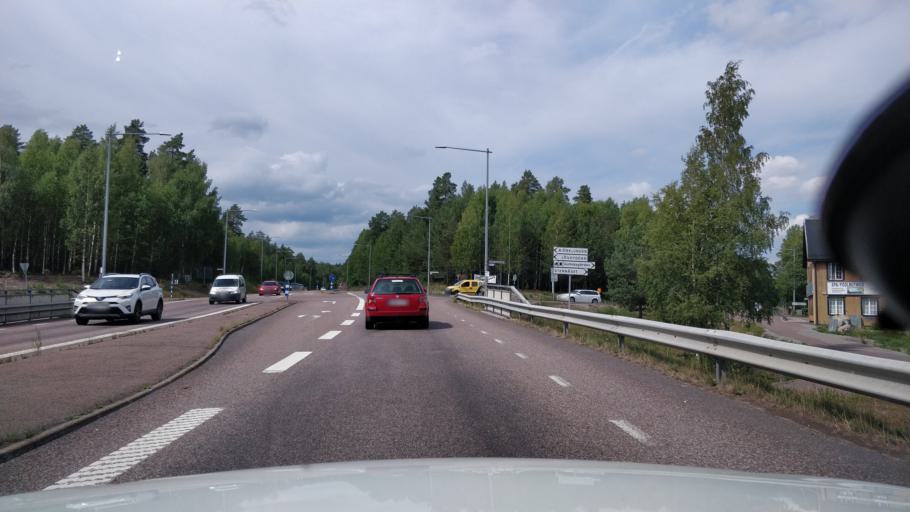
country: SE
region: Dalarna
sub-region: Faluns Kommun
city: Falun
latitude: 60.6285
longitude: 15.6031
